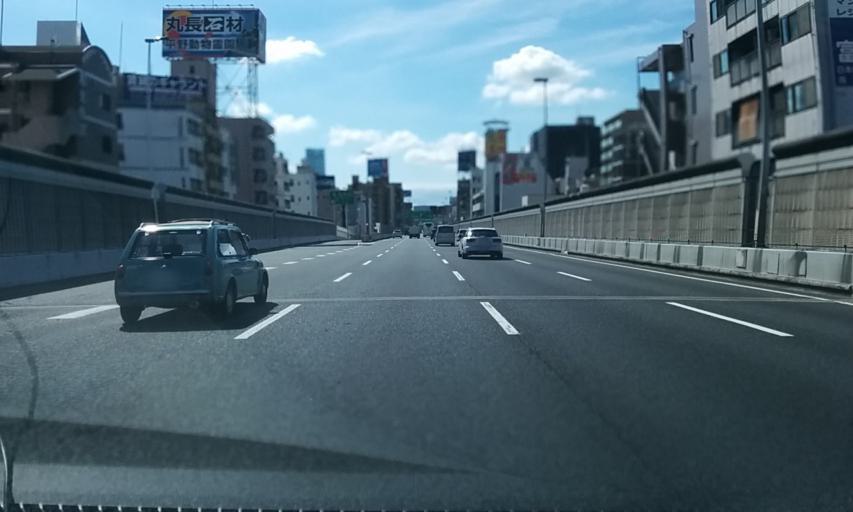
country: JP
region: Osaka
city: Osaka-shi
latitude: 34.6724
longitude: 135.5108
